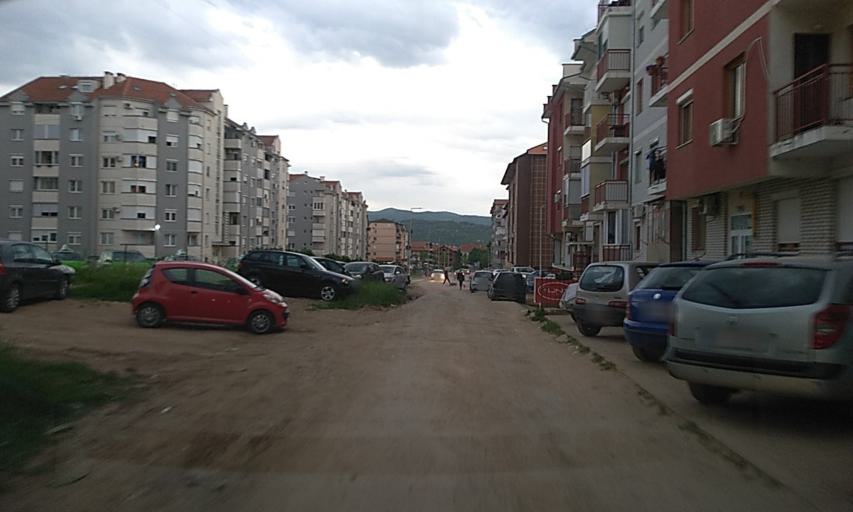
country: RS
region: Central Serbia
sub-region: Nisavski Okrug
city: Nis
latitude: 43.3385
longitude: 21.9227
